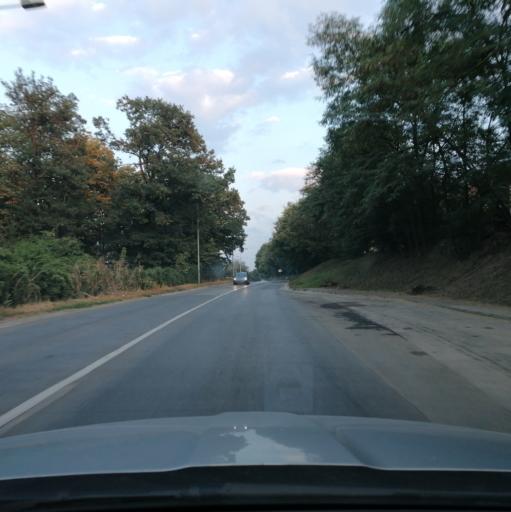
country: RS
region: Central Serbia
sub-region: Raski Okrug
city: Kraljevo
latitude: 43.7368
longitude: 20.6764
